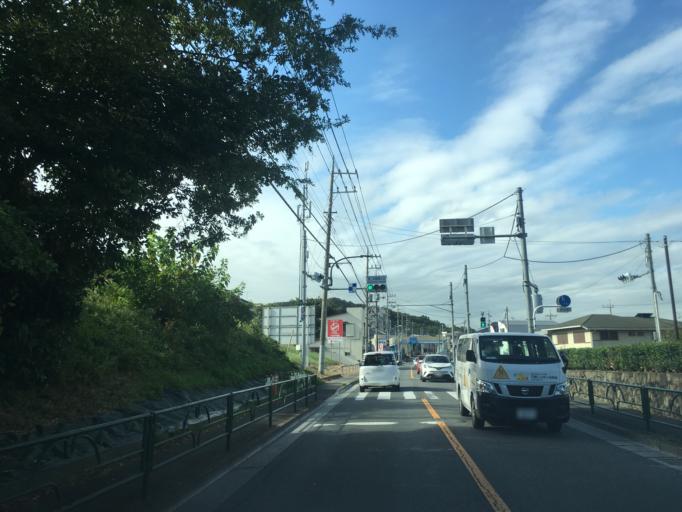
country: JP
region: Tokyo
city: Hino
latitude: 35.6495
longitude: 139.3882
